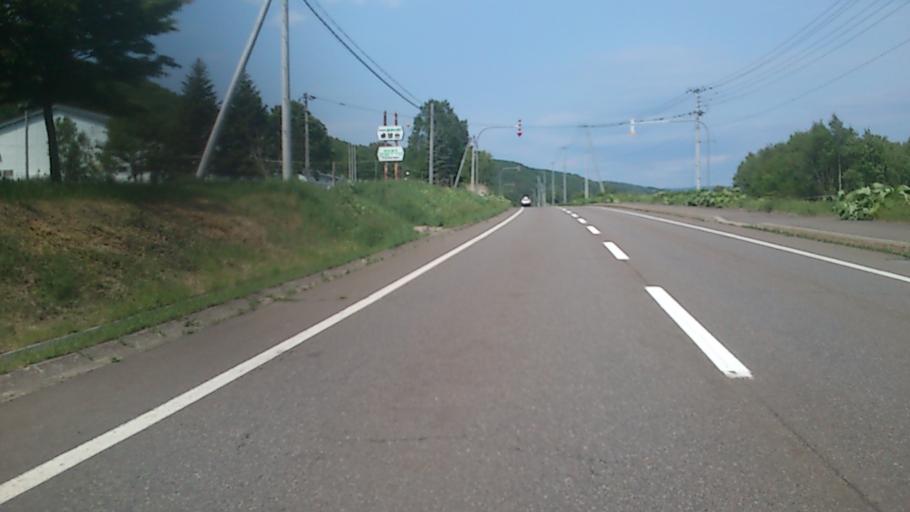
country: JP
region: Hokkaido
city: Otofuke
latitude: 43.2562
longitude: 143.5696
